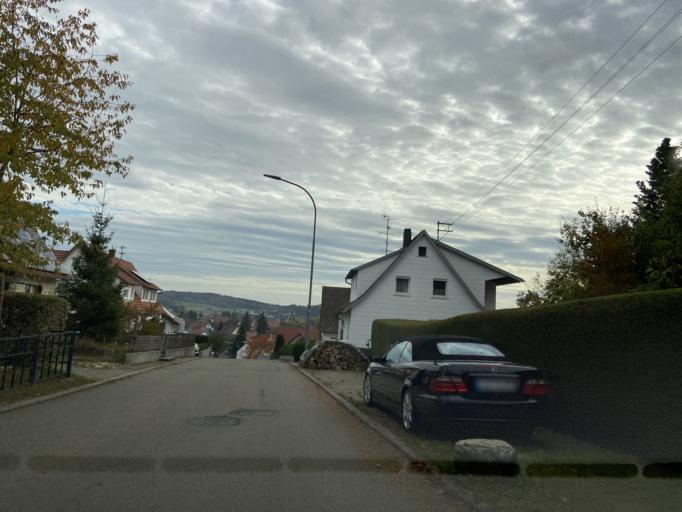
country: DE
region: Baden-Wuerttemberg
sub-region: Tuebingen Region
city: Bingen
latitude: 48.1106
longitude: 9.2656
